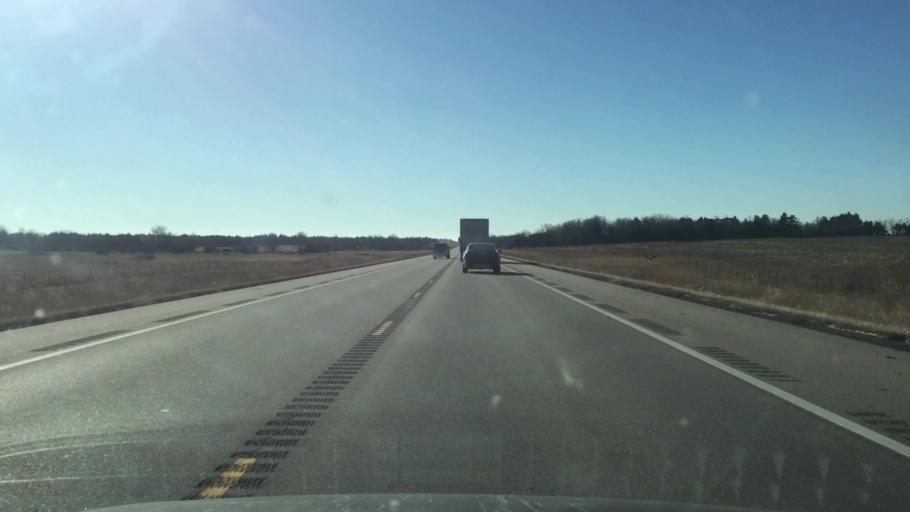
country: US
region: Kansas
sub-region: Allen County
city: Iola
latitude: 38.0425
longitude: -95.3805
